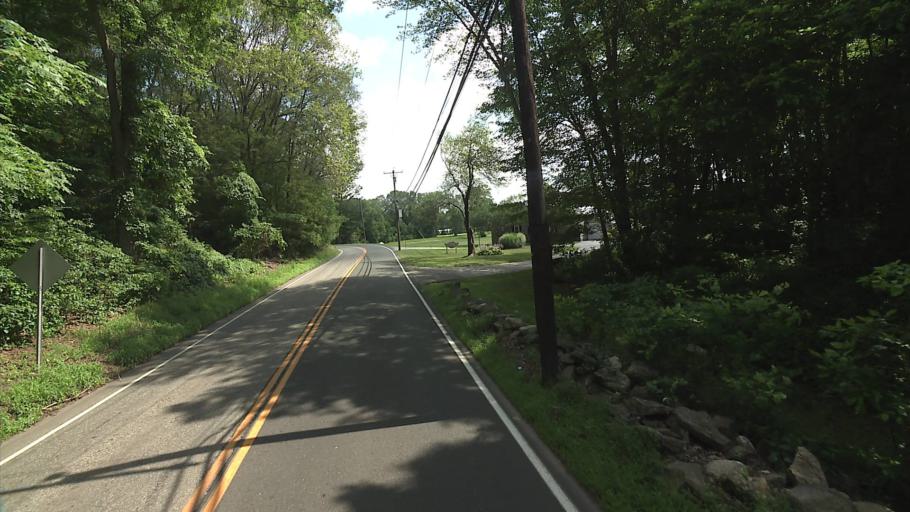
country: US
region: Connecticut
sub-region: Middlesex County
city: Essex Village
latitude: 41.3449
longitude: -72.4146
